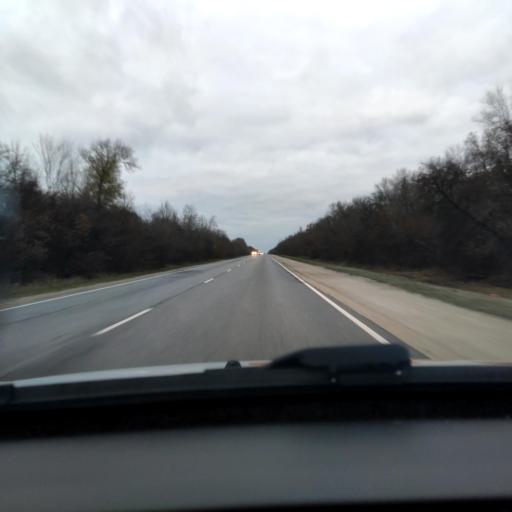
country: RU
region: Lipetsk
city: Khlevnoye
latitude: 52.3321
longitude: 39.1773
